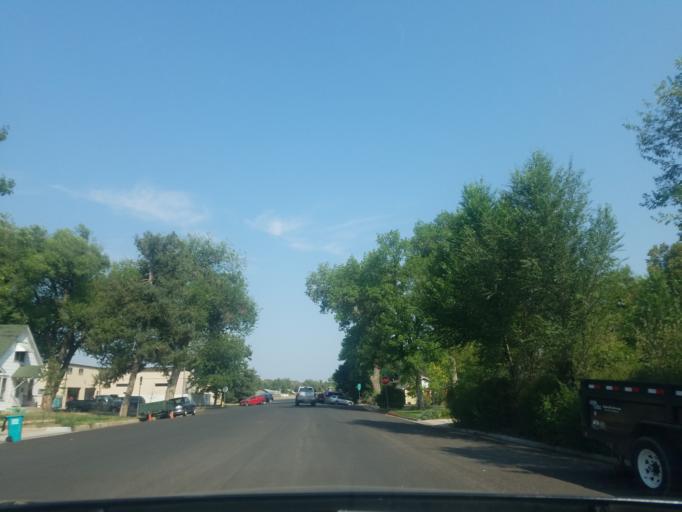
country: US
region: Colorado
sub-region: Larimer County
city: Fort Collins
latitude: 40.5828
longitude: -105.0673
